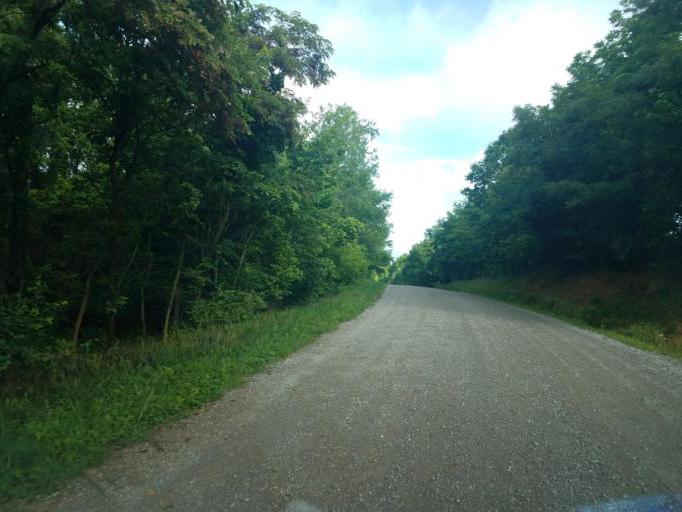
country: US
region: Ohio
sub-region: Gallia County
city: Gallipolis
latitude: 38.7447
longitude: -82.3481
